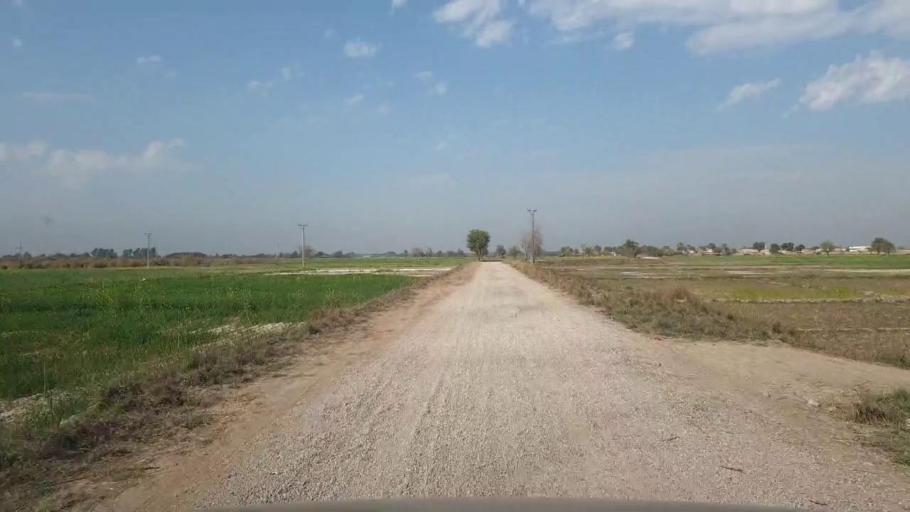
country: PK
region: Sindh
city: Sakrand
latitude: 26.0162
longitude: 68.4169
